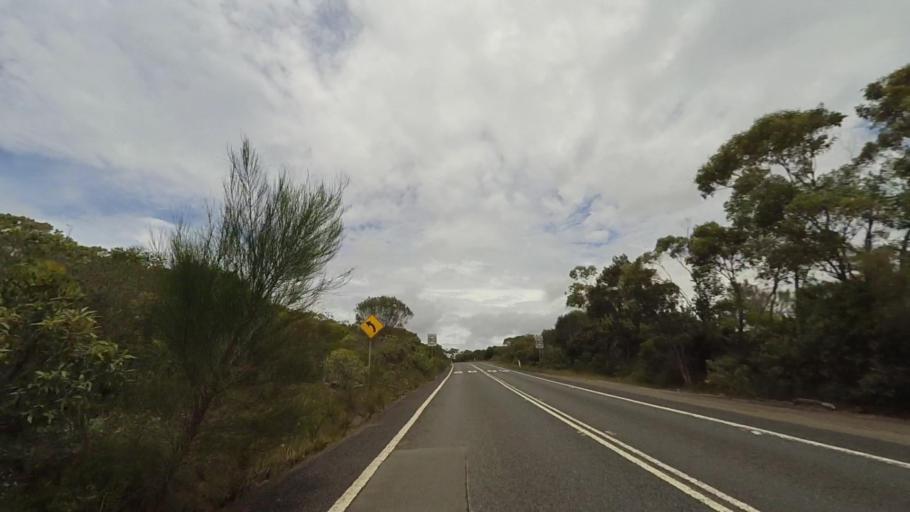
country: AU
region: New South Wales
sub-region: Sutherland Shire
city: Grays Point
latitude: -34.1226
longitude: 151.0791
